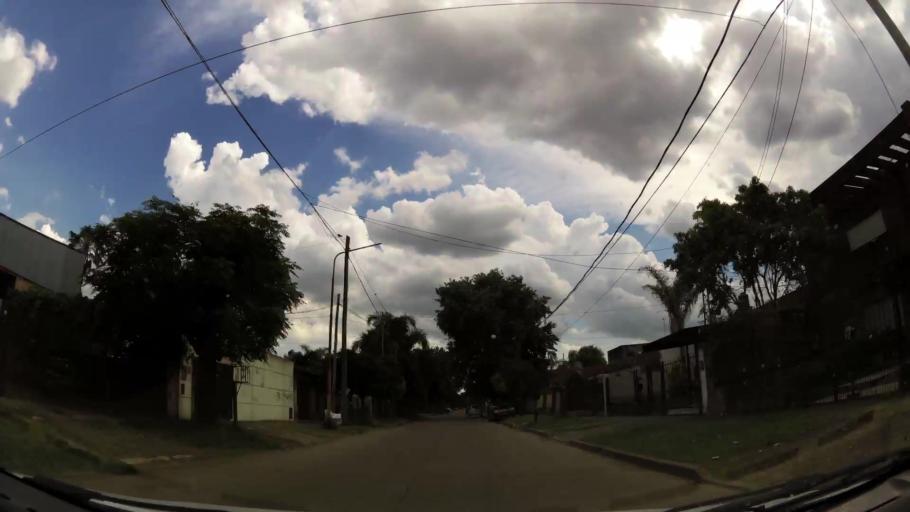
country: AR
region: Buenos Aires
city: Ituzaingo
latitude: -34.6382
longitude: -58.6772
